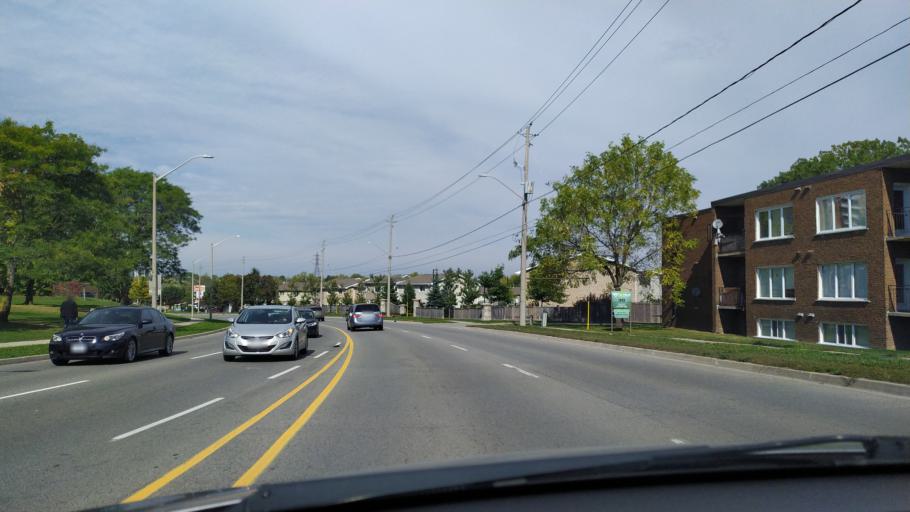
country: CA
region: Ontario
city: Kitchener
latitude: 43.4343
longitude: -80.5104
